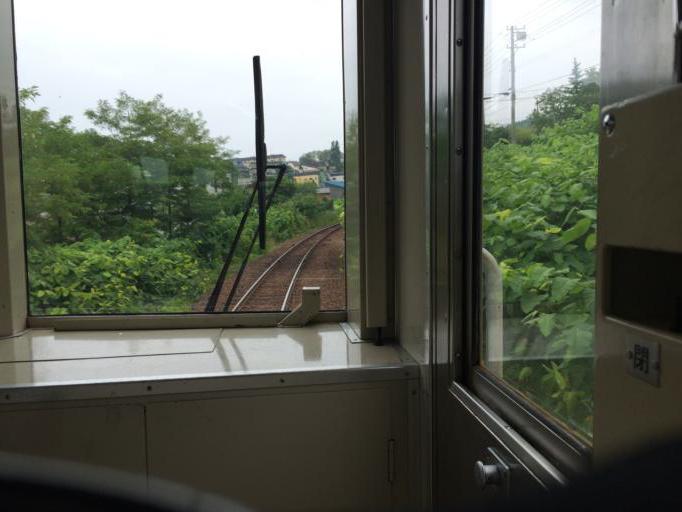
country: JP
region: Hokkaido
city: Otaru
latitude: 43.2057
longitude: 140.9832
